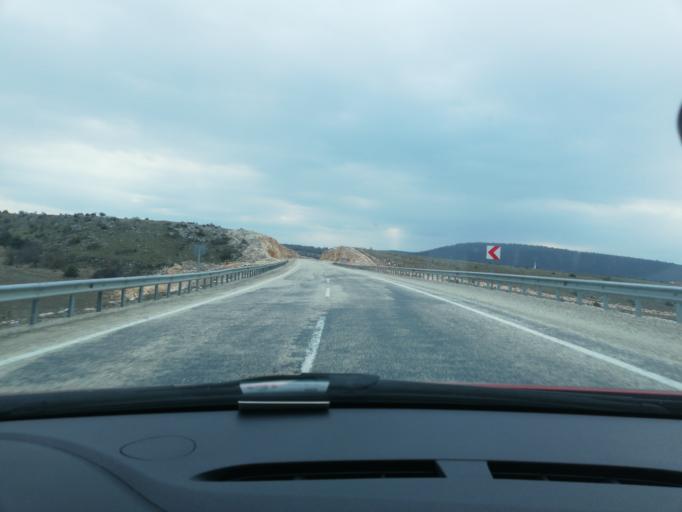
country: TR
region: Karabuk
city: Eflani
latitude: 41.4537
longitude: 33.0406
